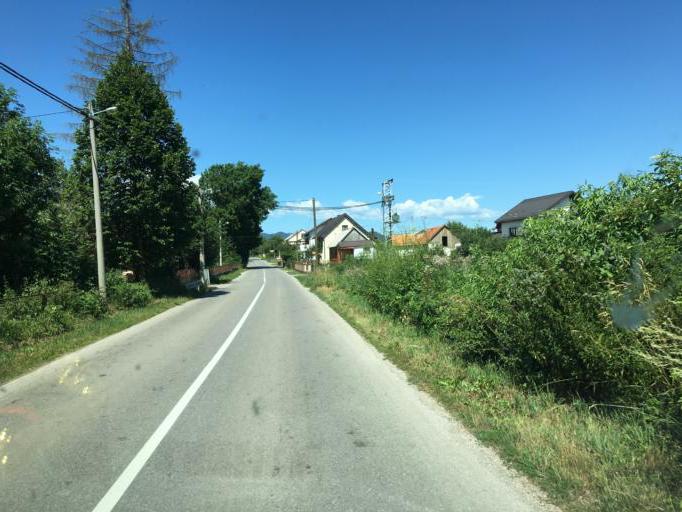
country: HR
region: Licko-Senjska
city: Gospic
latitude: 44.5539
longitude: 15.3503
